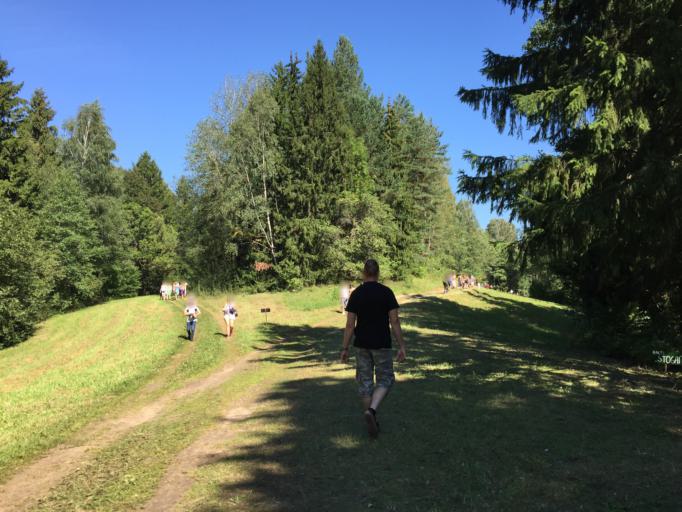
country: LT
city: Zarasai
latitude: 55.7902
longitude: 25.9652
